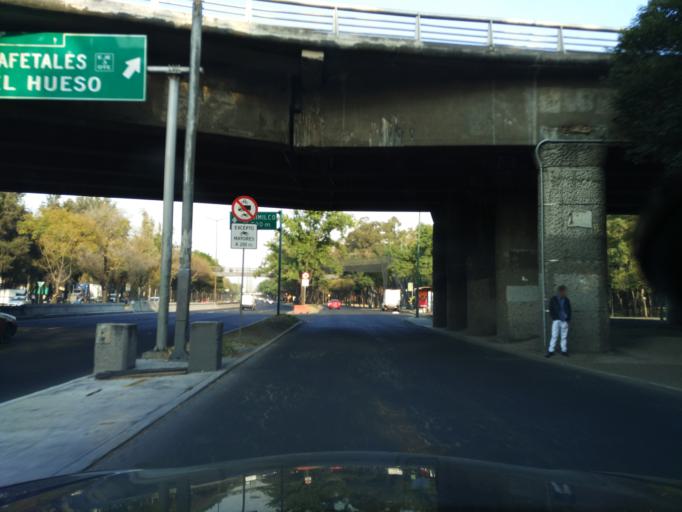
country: MX
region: Mexico City
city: Xochimilco
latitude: 19.2850
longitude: -99.1253
